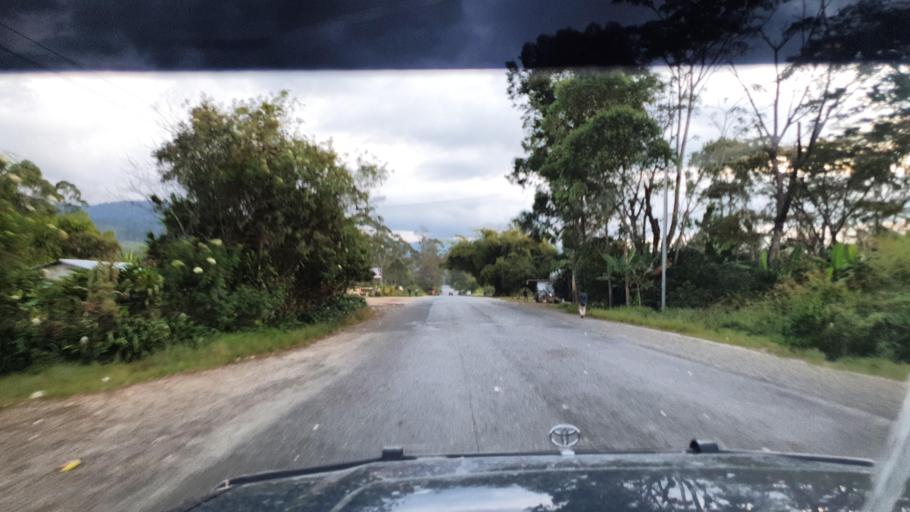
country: PG
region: Jiwaka
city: Minj
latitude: -5.8360
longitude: 144.5431
